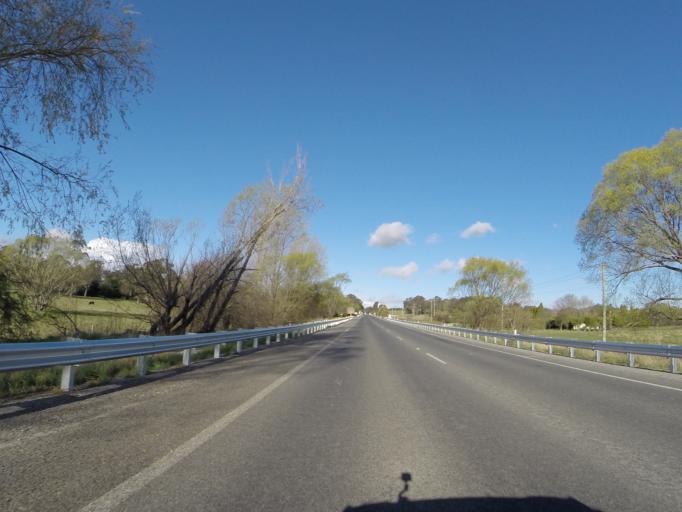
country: AU
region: New South Wales
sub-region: Wingecarribee
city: Moss Vale
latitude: -34.5738
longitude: 150.4689
